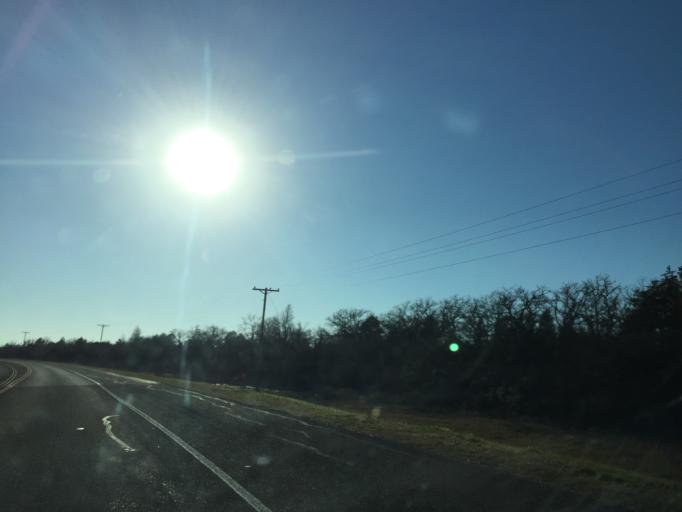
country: US
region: Texas
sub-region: Bastrop County
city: Elgin
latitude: 30.3750
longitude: -97.2584
